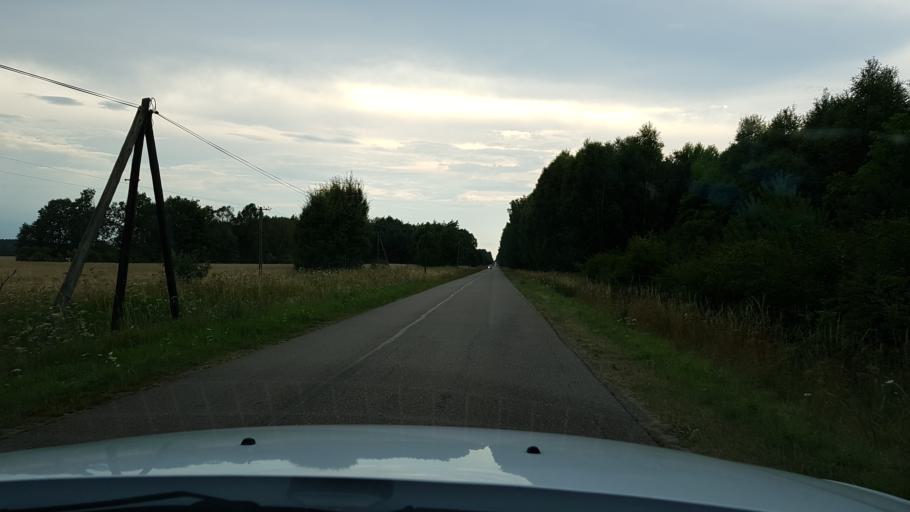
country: PL
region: West Pomeranian Voivodeship
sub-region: Powiat drawski
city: Czaplinek
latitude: 53.4438
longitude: 16.2526
